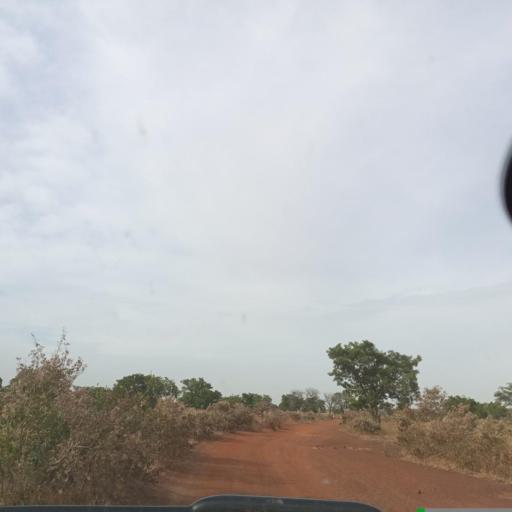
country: ML
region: Koulikoro
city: Koulikoro
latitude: 13.1088
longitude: -7.6199
